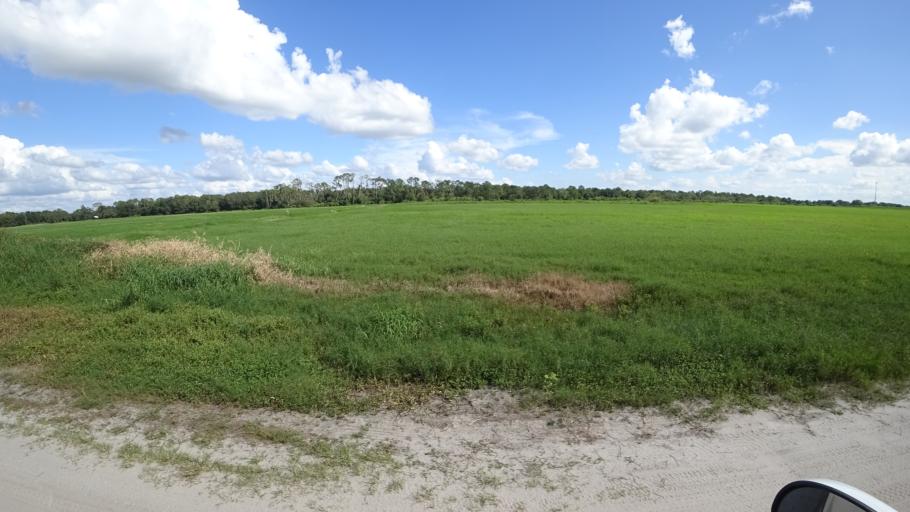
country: US
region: Florida
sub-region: DeSoto County
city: Arcadia
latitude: 27.3183
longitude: -82.1247
